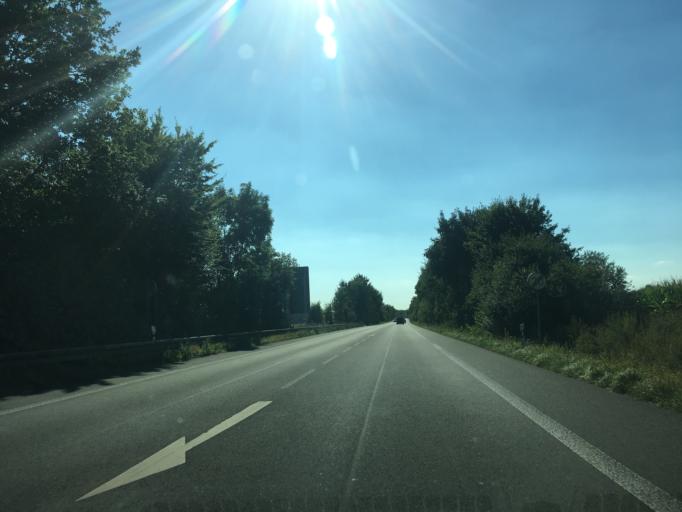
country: DE
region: North Rhine-Westphalia
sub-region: Regierungsbezirk Detmold
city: Rheda-Wiedenbruck
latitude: 51.8781
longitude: 8.2818
